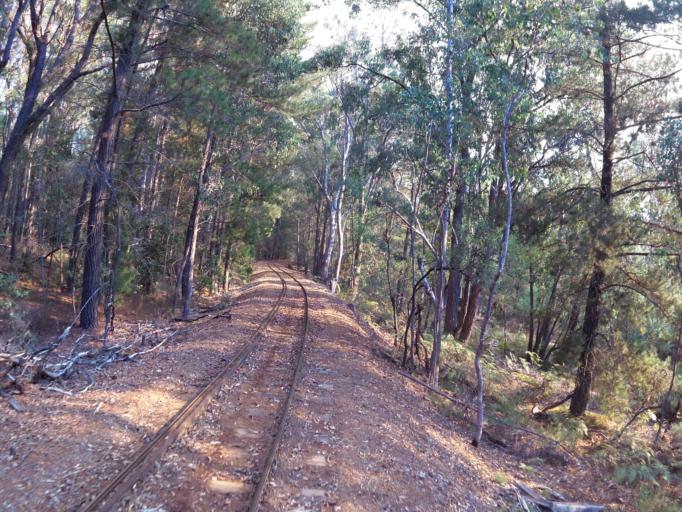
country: AU
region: Western Australia
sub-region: Waroona
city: Waroona
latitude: -32.7374
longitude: 116.1312
